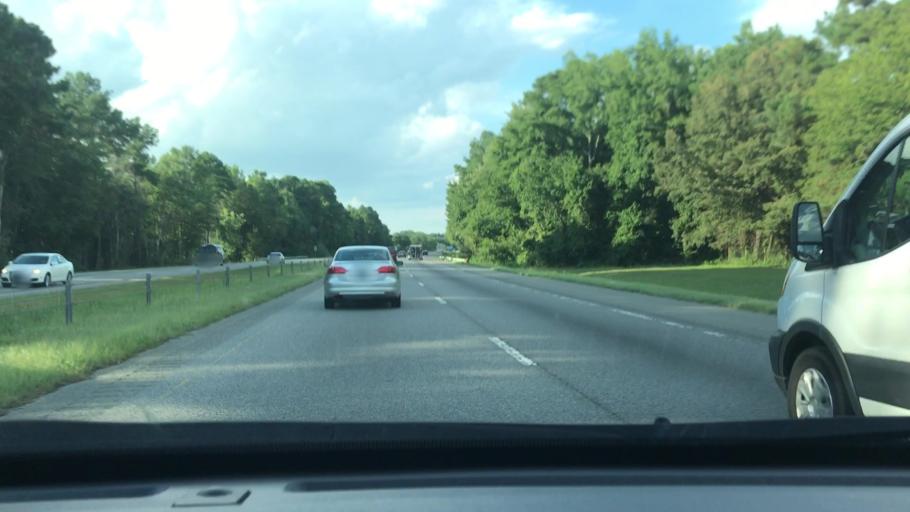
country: US
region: North Carolina
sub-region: Cumberland County
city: Hope Mills
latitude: 34.9084
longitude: -78.9561
